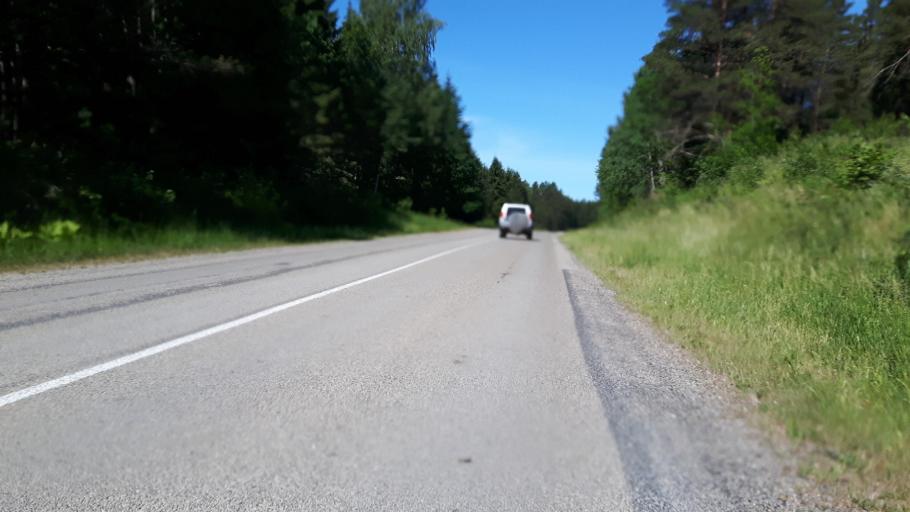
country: LV
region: Tukuma Rajons
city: Tukums
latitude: 57.0053
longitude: 23.0685
